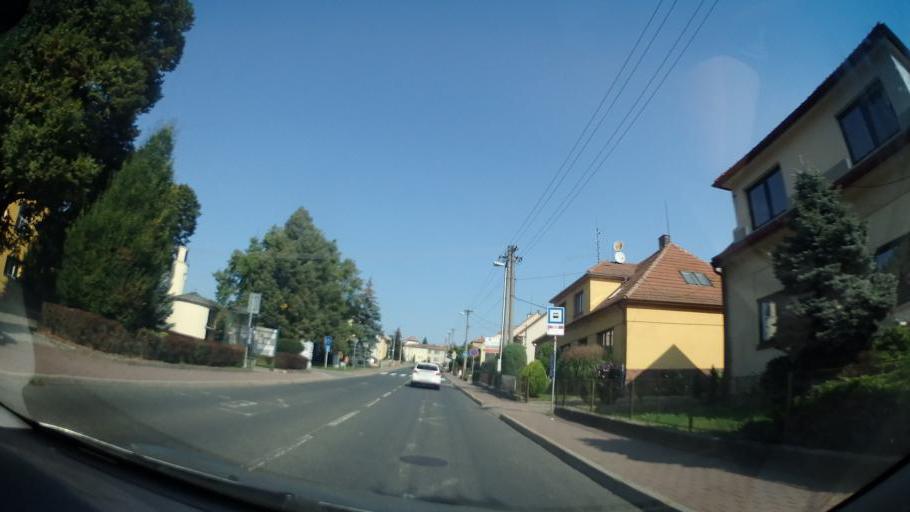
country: CZ
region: South Moravian
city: Kurim
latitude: 49.2358
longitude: 16.5281
